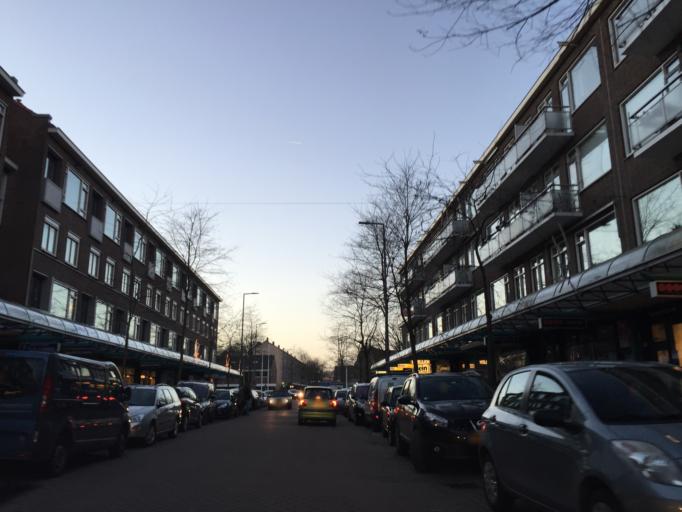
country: NL
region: South Holland
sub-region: Gemeente Lansingerland
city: Berkel en Rodenrijs
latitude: 51.9600
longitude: 4.4712
